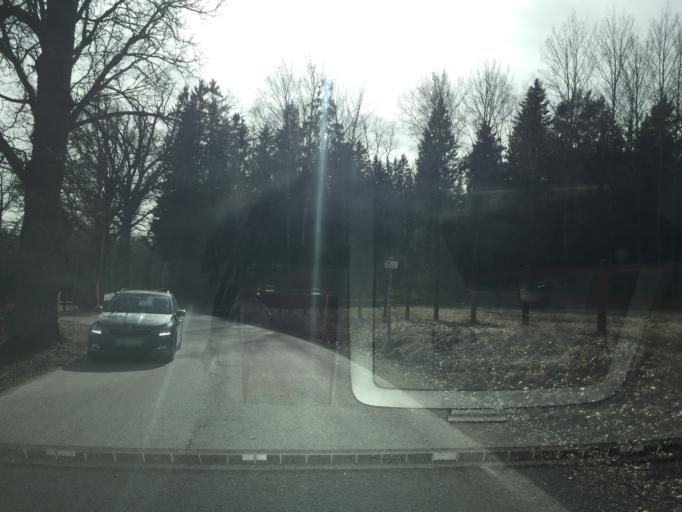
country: SE
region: Stockholm
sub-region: Botkyrka Kommun
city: Tullinge
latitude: 59.1073
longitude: 17.9749
